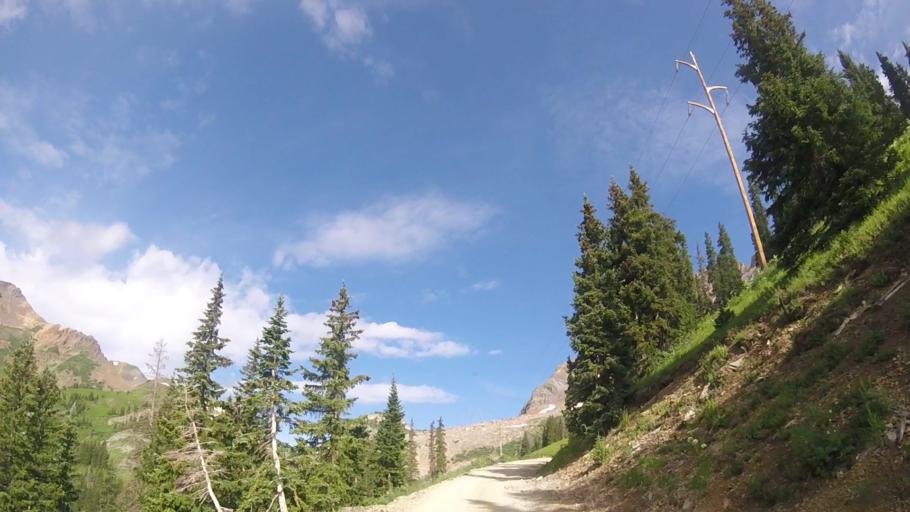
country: US
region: Colorado
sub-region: San Miguel County
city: Telluride
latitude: 37.8496
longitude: -107.7695
